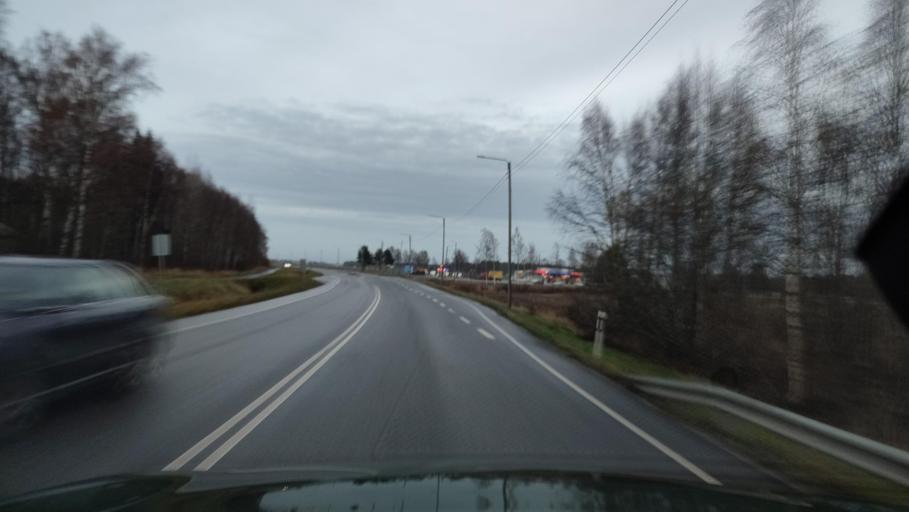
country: FI
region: Ostrobothnia
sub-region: Vaasa
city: Ristinummi
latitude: 63.0402
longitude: 21.7416
